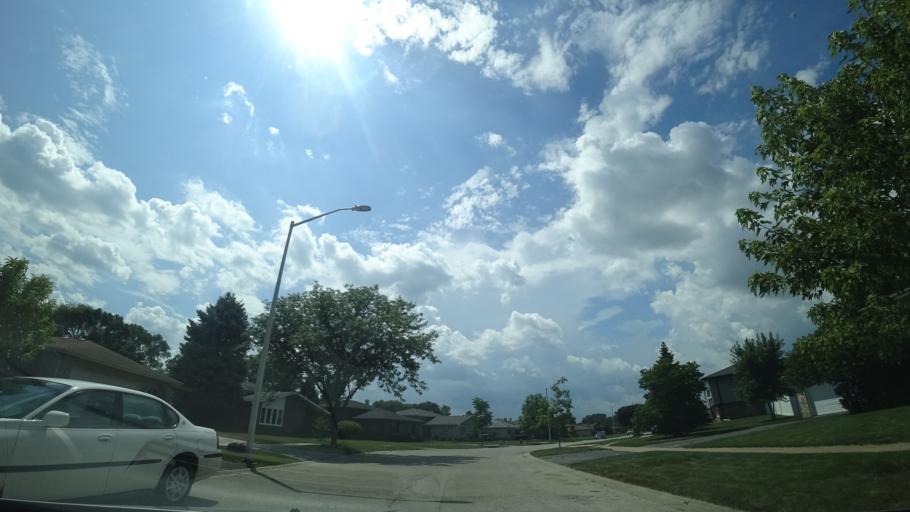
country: US
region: Illinois
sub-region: Cook County
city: Alsip
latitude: 41.6717
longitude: -87.7227
